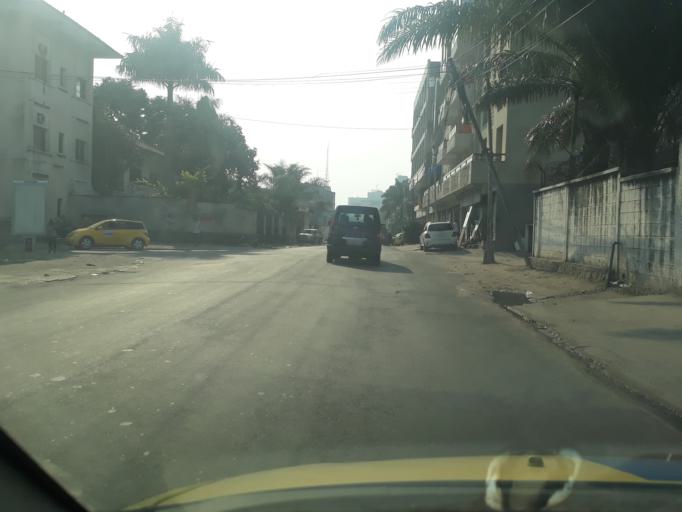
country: CD
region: Kinshasa
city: Kinshasa
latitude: -4.3064
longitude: 15.3239
